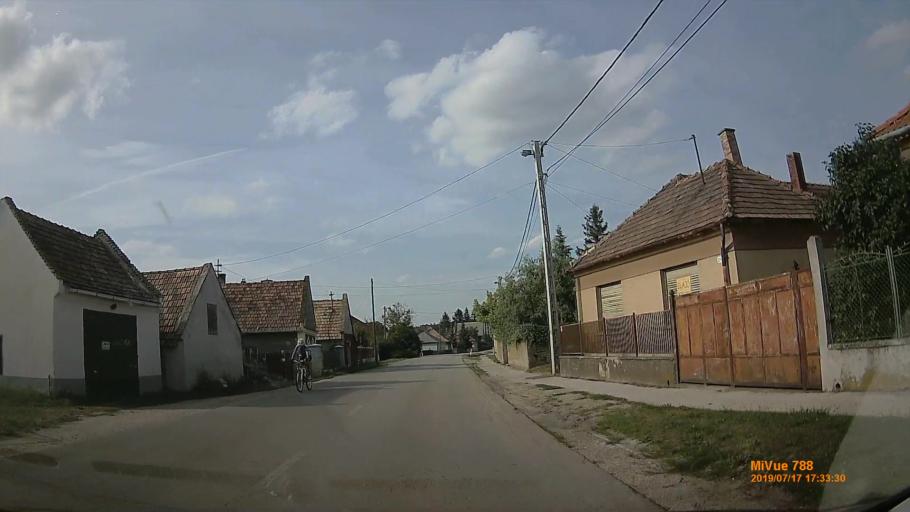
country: HU
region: Veszprem
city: Ajka
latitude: 47.0492
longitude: 17.5541
